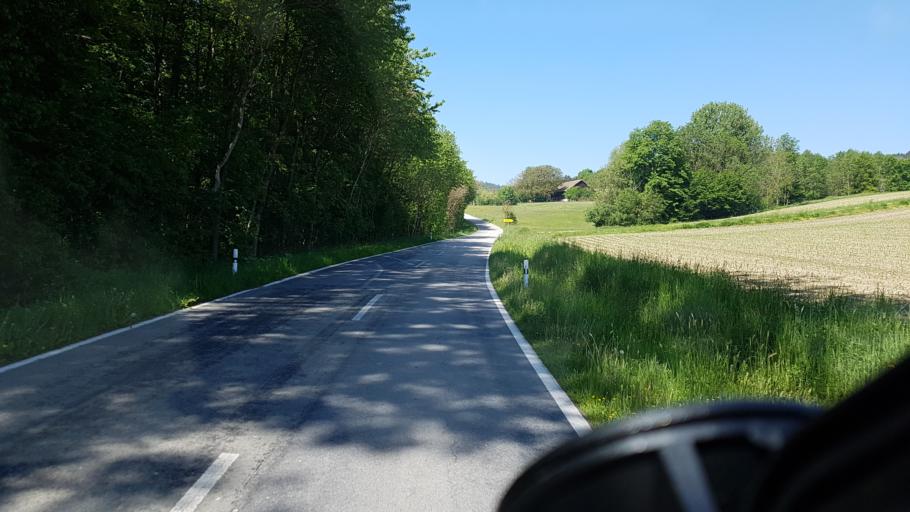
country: DE
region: Bavaria
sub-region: Lower Bavaria
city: Stubenberg
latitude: 48.2940
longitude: 13.0718
